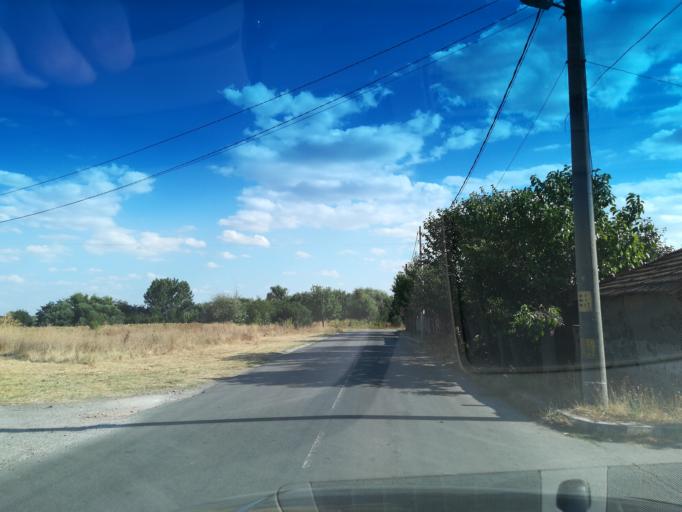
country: BG
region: Khaskovo
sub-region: Obshtina Mineralni Bani
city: Mineralni Bani
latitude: 42.0212
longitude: 25.4304
